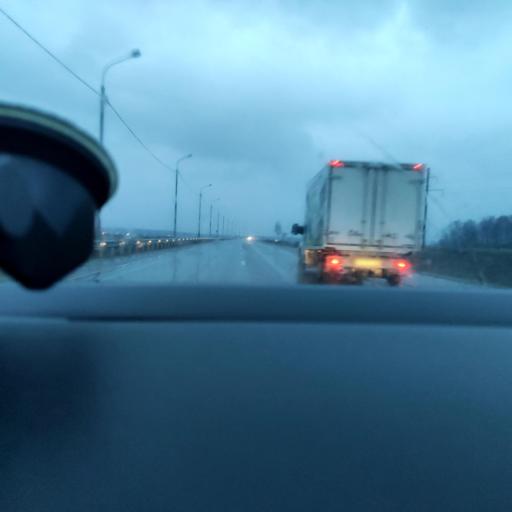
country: RU
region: Moskovskaya
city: Yegor'yevsk
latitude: 55.3948
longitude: 39.0687
